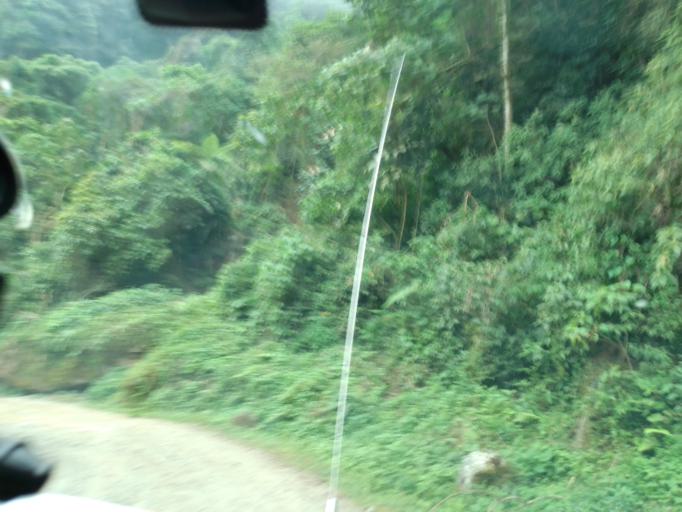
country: MX
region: Chiapas
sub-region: Union Juarez
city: Santo Domingo
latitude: 15.0913
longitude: -92.0976
